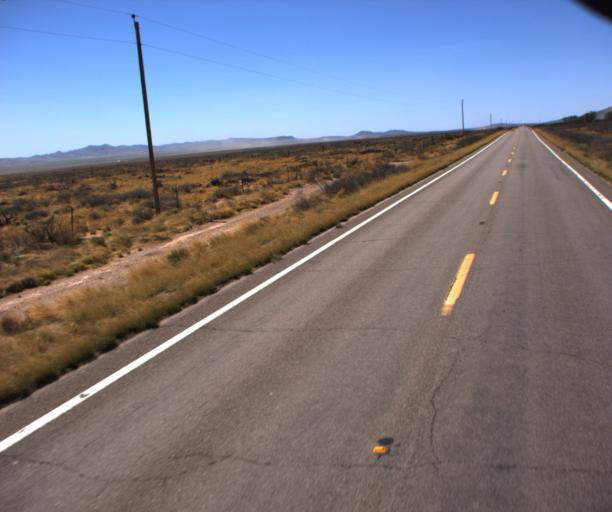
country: US
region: Arizona
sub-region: Cochise County
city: Douglas
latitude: 31.7645
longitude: -109.0814
